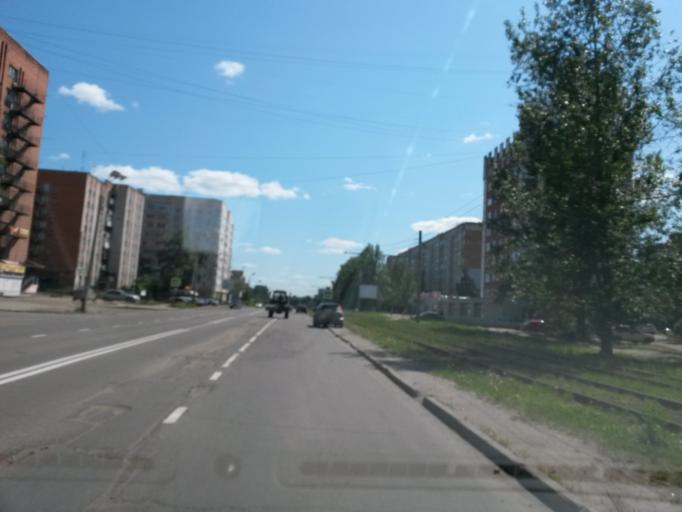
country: RU
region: Jaroslavl
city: Yaroslavl
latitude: 57.6885
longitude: 39.7618
